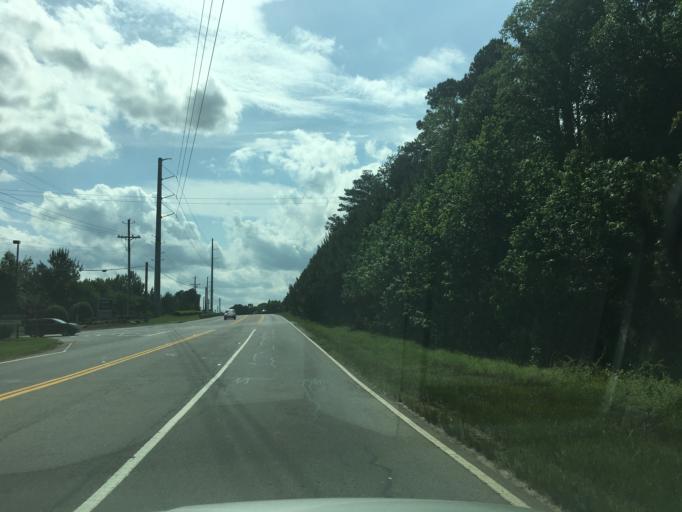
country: US
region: Georgia
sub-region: Jackson County
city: Braselton
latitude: 34.1049
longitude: -83.7785
